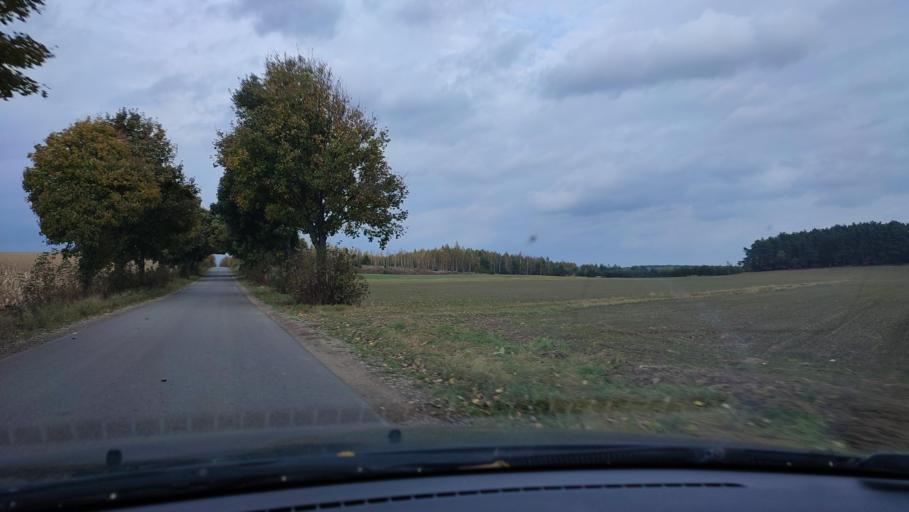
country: PL
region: Masovian Voivodeship
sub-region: Powiat mlawski
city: Mlawa
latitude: 53.1942
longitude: 20.3833
